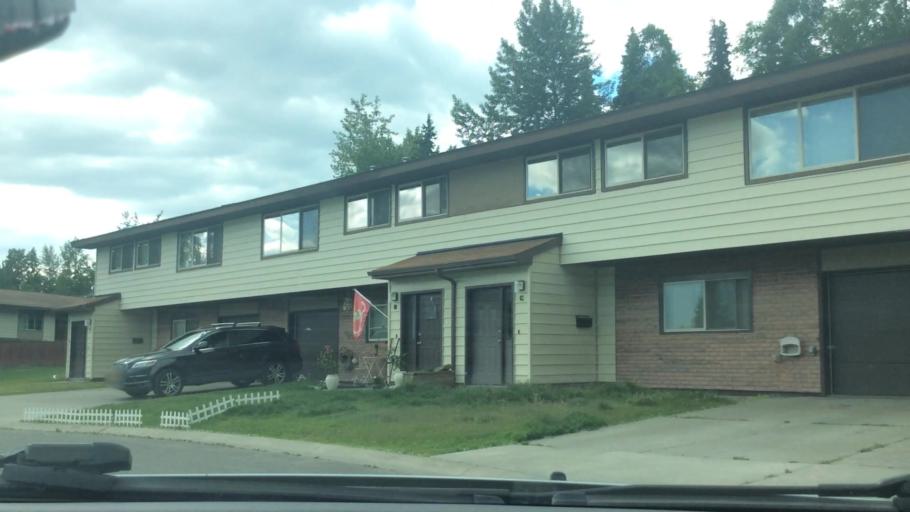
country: US
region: Alaska
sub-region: Anchorage Municipality
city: Elmendorf Air Force Base
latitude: 61.2304
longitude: -149.7519
